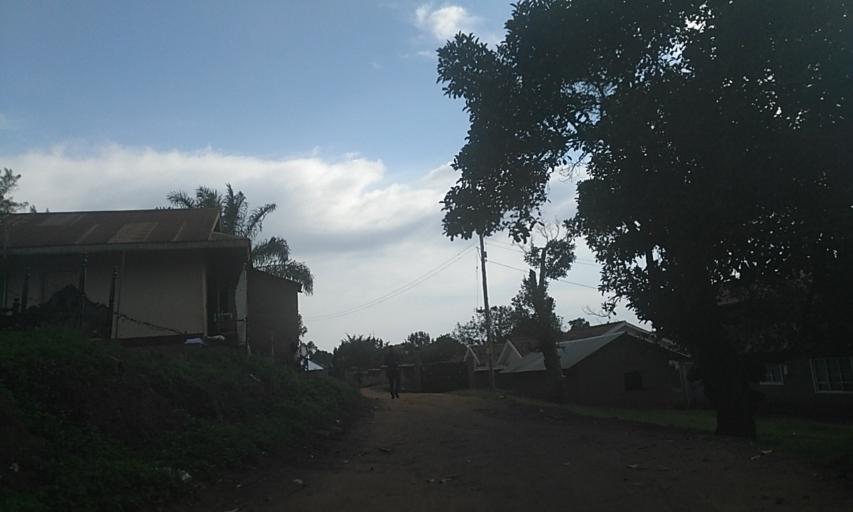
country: UG
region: Central Region
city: Kampala Central Division
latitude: 0.3183
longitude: 32.5565
